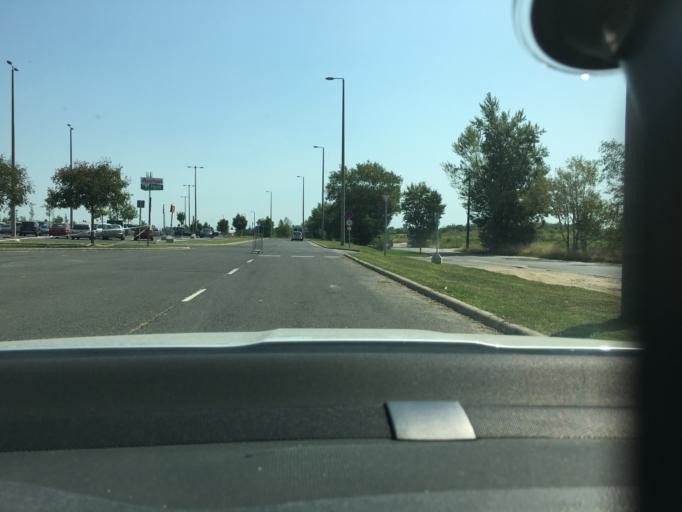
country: HU
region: Pest
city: Csomor
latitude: 47.5406
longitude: 19.2418
